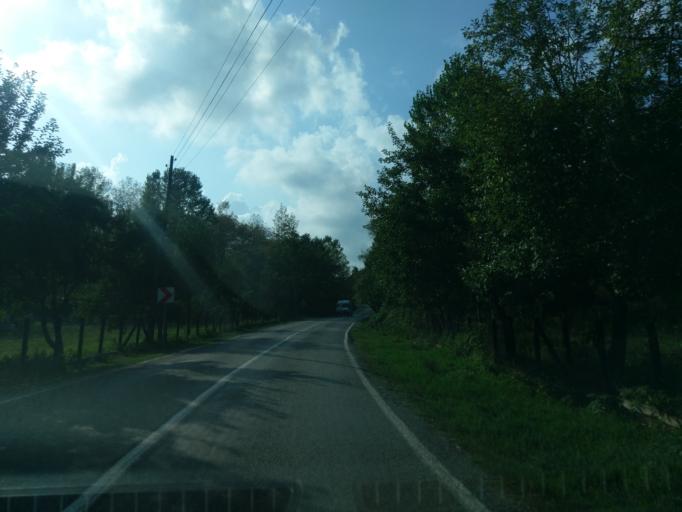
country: TR
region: Sinop
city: Helaldi
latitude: 41.9002
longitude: 34.4610
